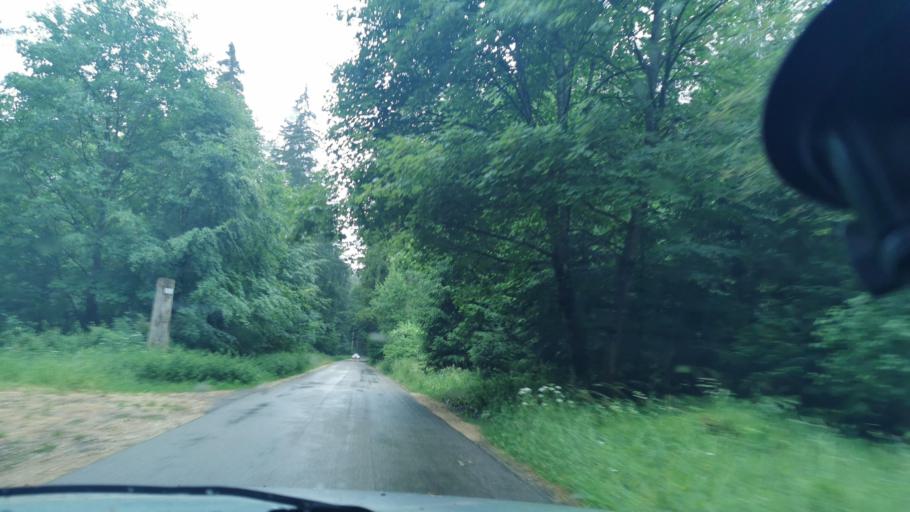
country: DE
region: Baden-Wuerttemberg
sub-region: Regierungsbezirk Stuttgart
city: Bohmenkirch
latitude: 48.7217
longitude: 9.9369
